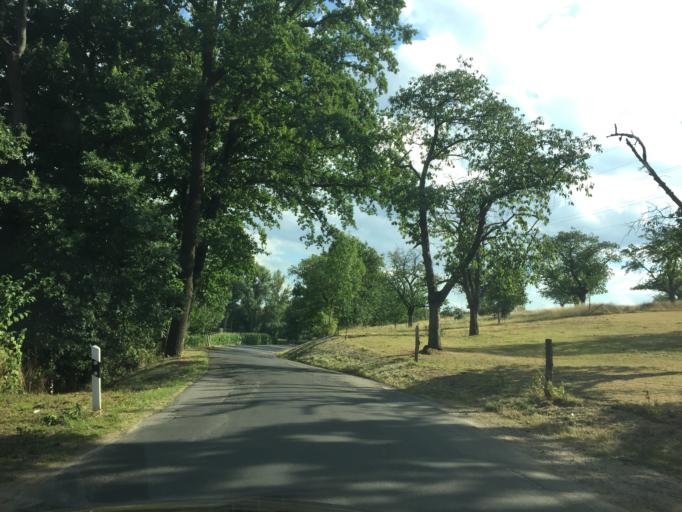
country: DE
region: Thuringia
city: Nobitz
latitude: 50.9713
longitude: 12.4667
